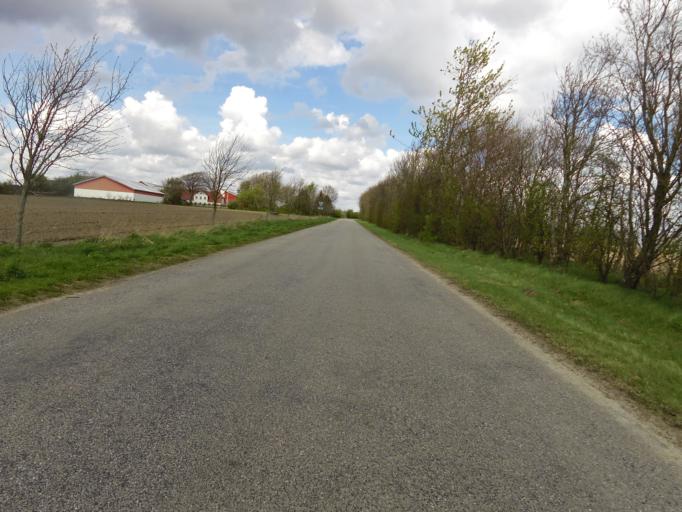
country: DK
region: South Denmark
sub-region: Tonder Kommune
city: Toftlund
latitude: 55.2049
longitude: 9.1463
